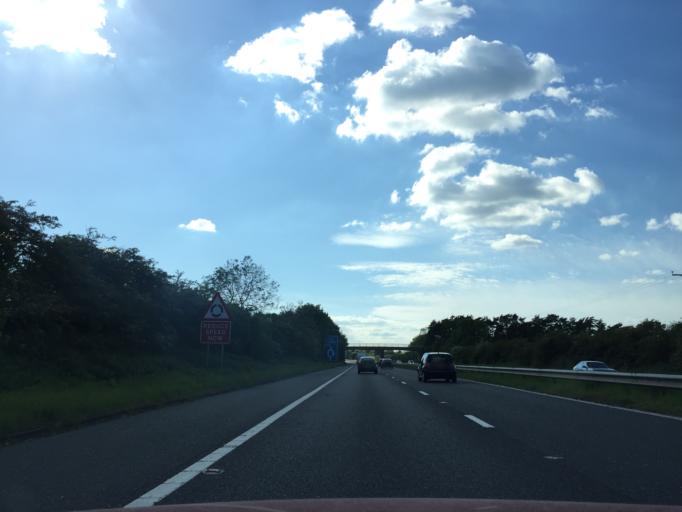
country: GB
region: England
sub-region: Warwickshire
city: Dunchurch
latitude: 52.3376
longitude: -1.3103
